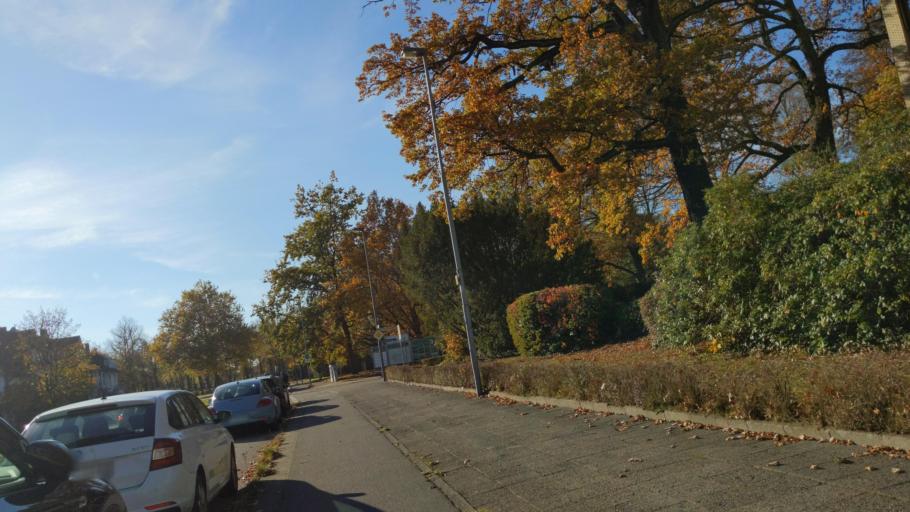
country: DE
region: Schleswig-Holstein
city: Luebeck
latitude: 53.8812
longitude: 10.6998
